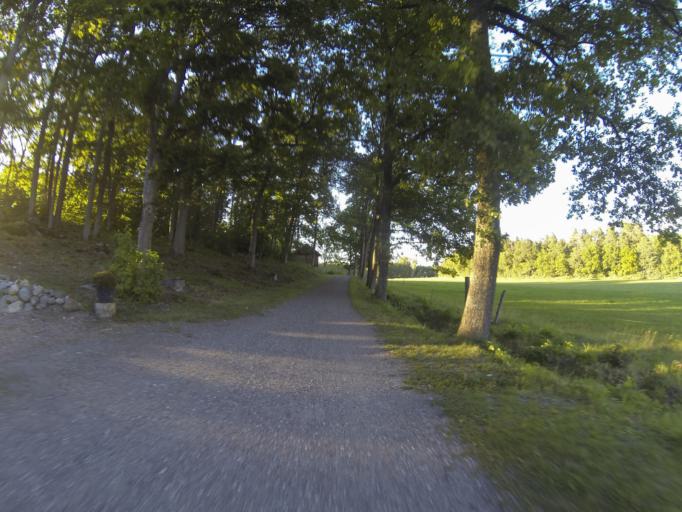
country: SE
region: Vaestmanland
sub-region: Vasteras
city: Vasteras
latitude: 59.5519
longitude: 16.6624
